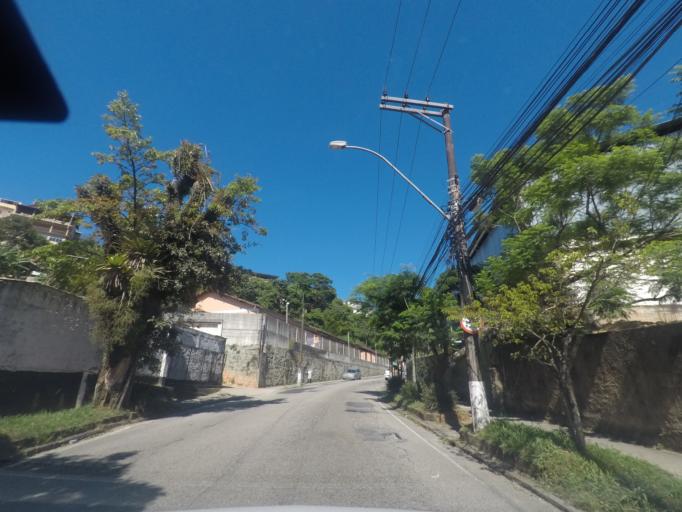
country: BR
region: Rio de Janeiro
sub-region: Petropolis
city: Petropolis
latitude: -22.5277
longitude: -43.1774
